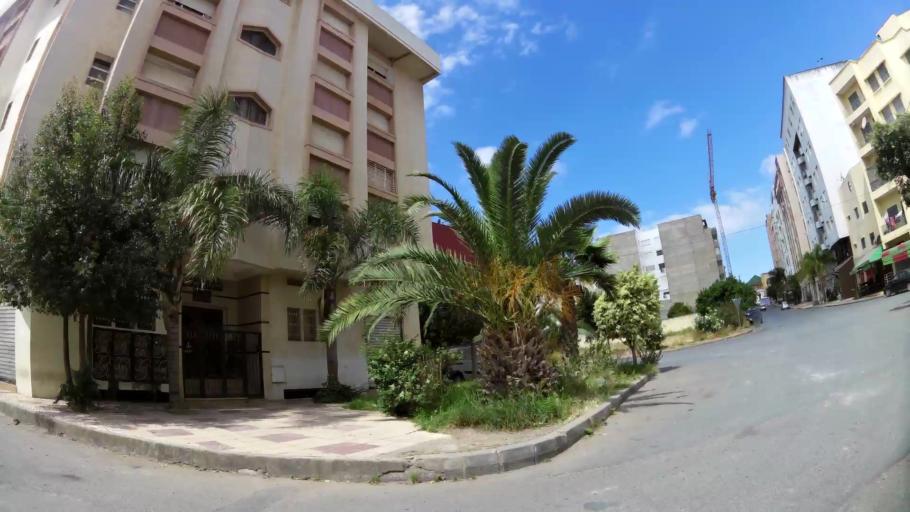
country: MA
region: Gharb-Chrarda-Beni Hssen
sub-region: Kenitra Province
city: Kenitra
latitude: 34.2527
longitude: -6.5935
